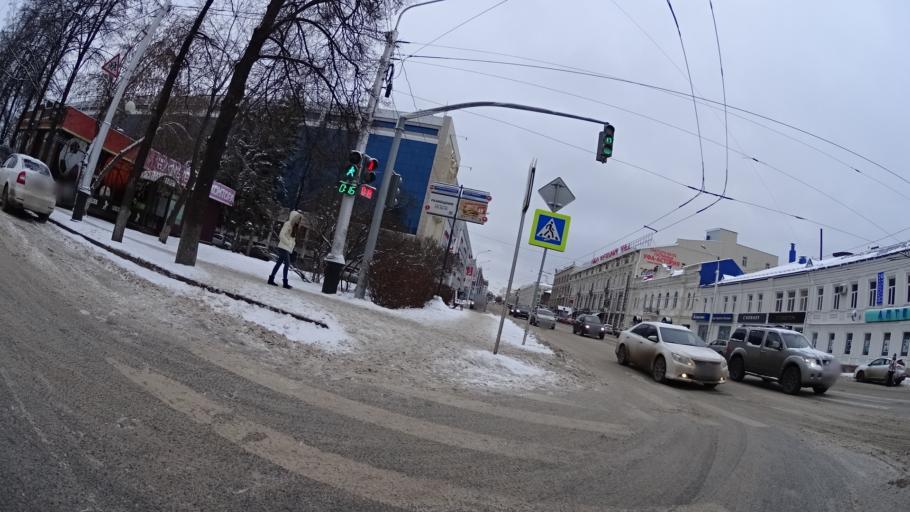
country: RU
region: Bashkortostan
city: Ufa
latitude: 54.7270
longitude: 55.9418
